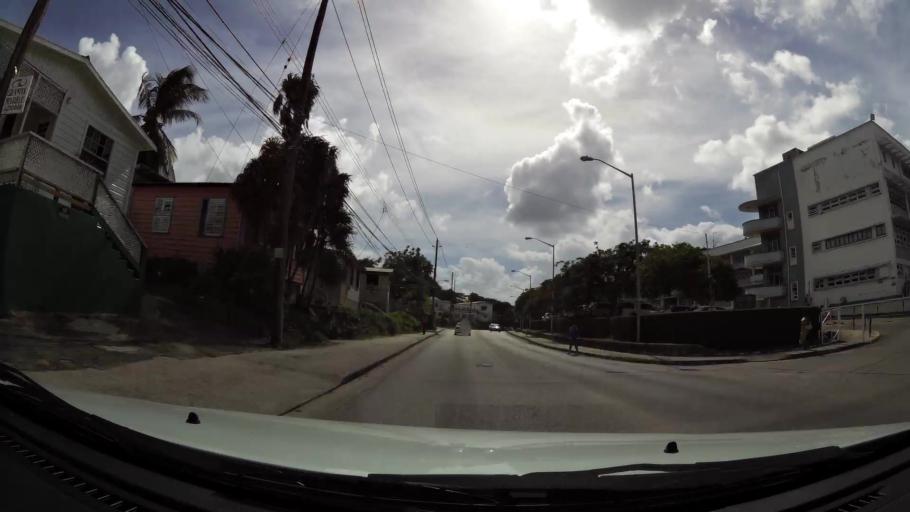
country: BB
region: Saint Michael
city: Bridgetown
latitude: 13.0950
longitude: -59.6062
